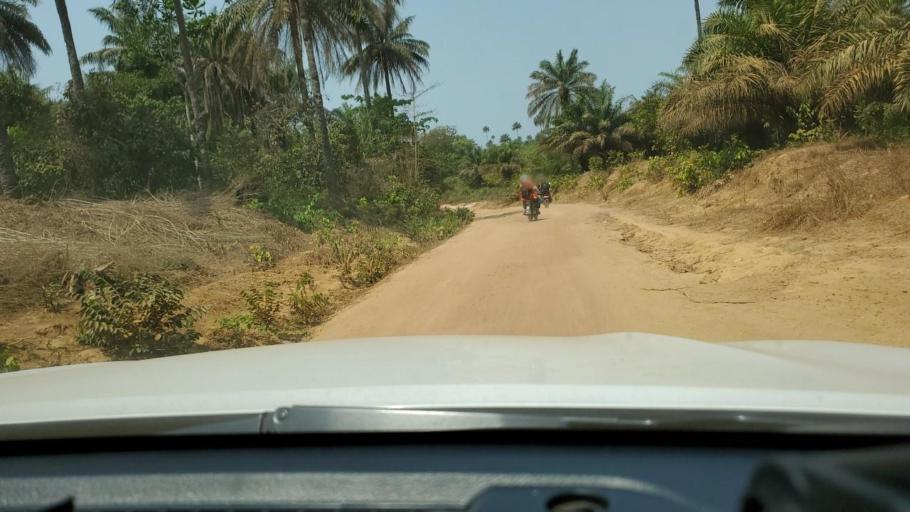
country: GN
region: Boke
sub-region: Boffa
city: Boffa
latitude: 10.0811
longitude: -13.8652
